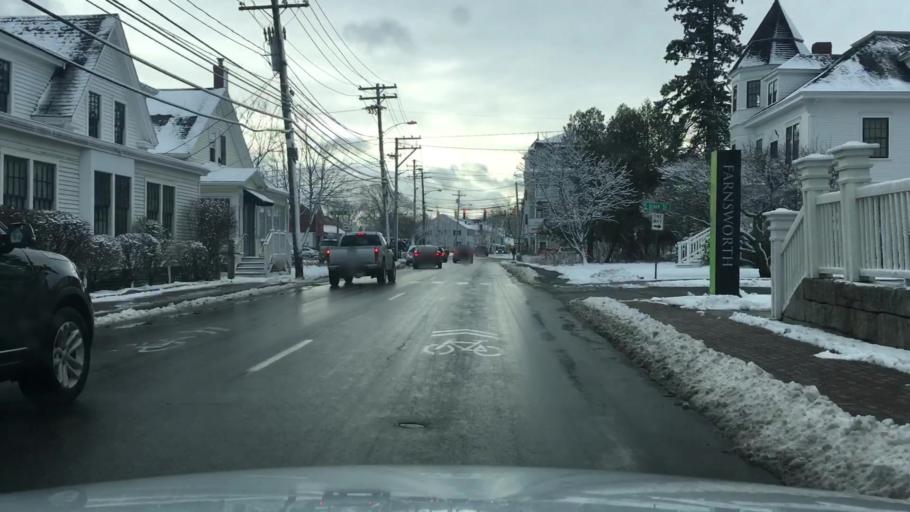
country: US
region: Maine
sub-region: Knox County
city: Rockland
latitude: 44.1032
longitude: -69.1109
